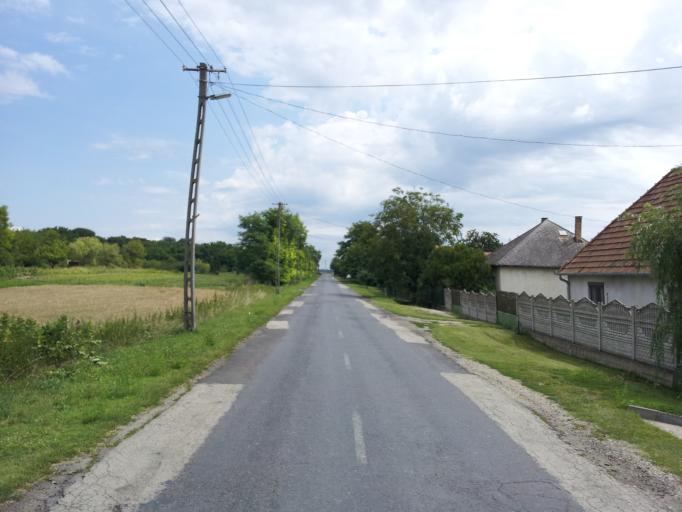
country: HU
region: Pest
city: Kiskunlachaza
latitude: 47.2337
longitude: 19.0159
